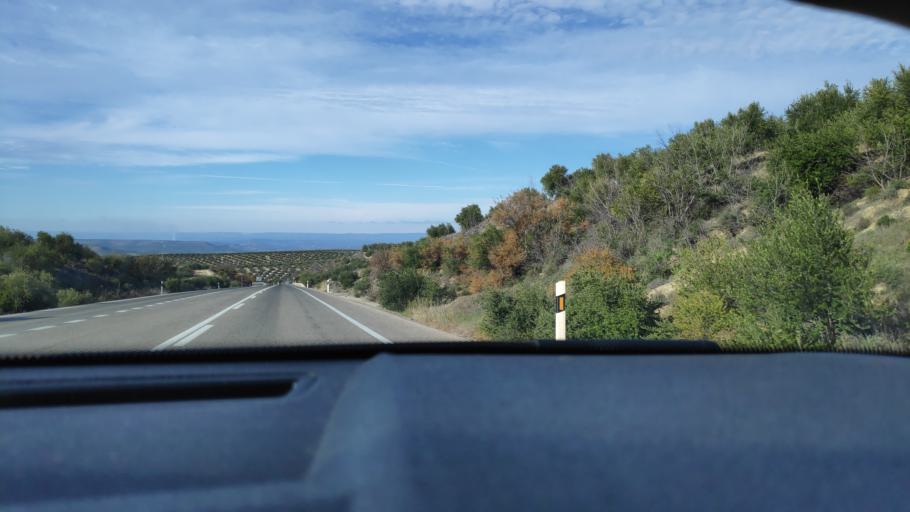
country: ES
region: Andalusia
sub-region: Provincia de Jaen
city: Porcuna
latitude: 37.8764
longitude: -4.1742
